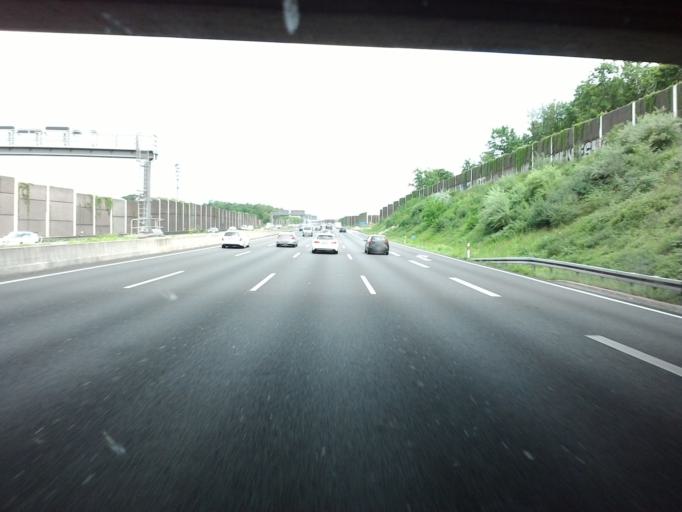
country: DE
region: North Rhine-Westphalia
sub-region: Regierungsbezirk Koln
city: Buchheim
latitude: 50.9667
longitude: 7.0314
